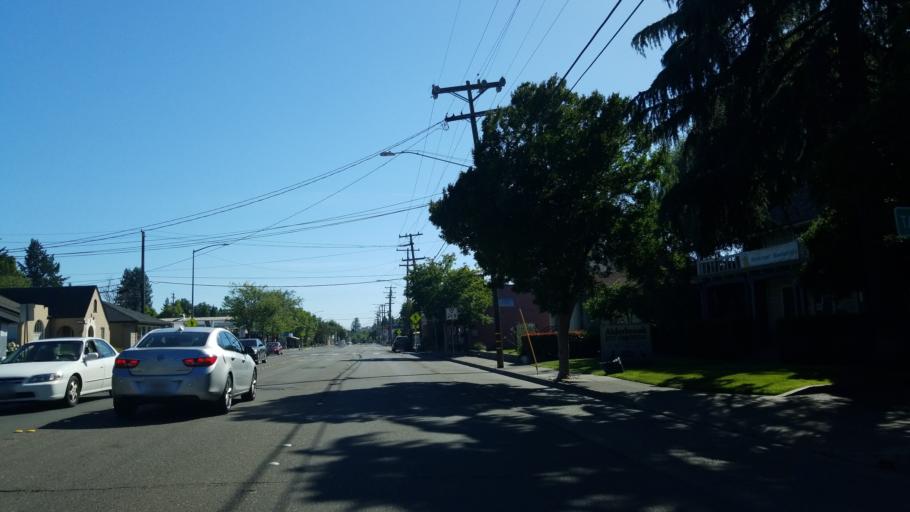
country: US
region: California
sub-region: Sonoma County
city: Santa Rosa
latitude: 38.4480
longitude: -122.7003
